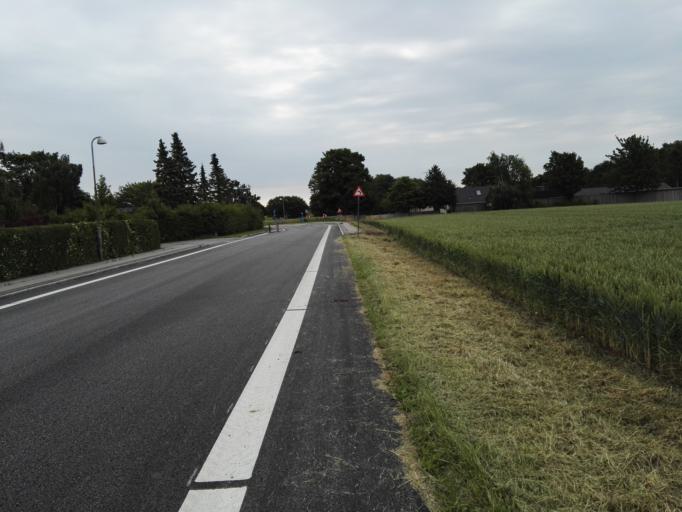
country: DK
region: Zealand
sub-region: Roskilde Kommune
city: Jyllinge
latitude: 55.7450
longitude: 12.1191
